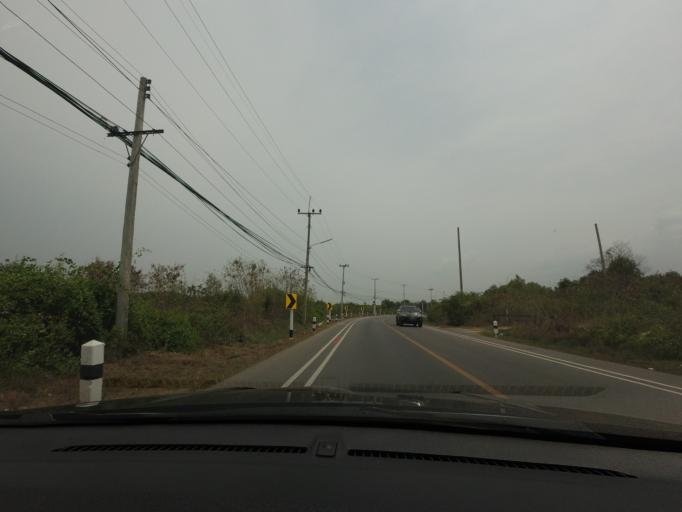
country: TH
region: Ratchaburi
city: Pak Tho
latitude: 13.3064
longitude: 99.9106
